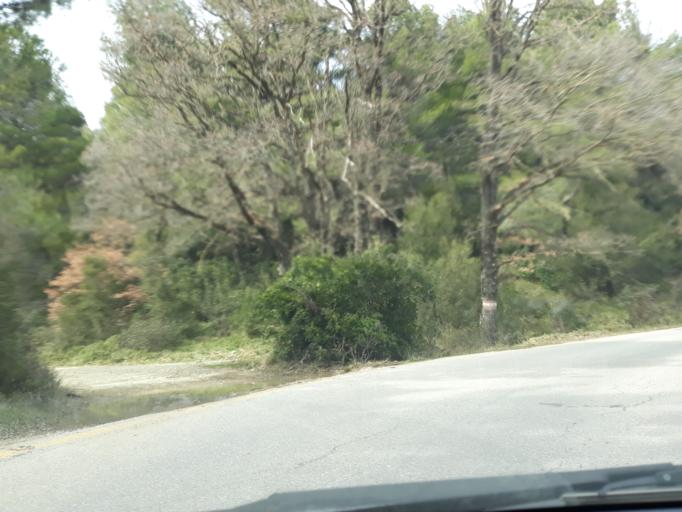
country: GR
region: Attica
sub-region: Nomarchia Anatolikis Attikis
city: Varybobi
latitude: 38.1724
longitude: 23.7899
